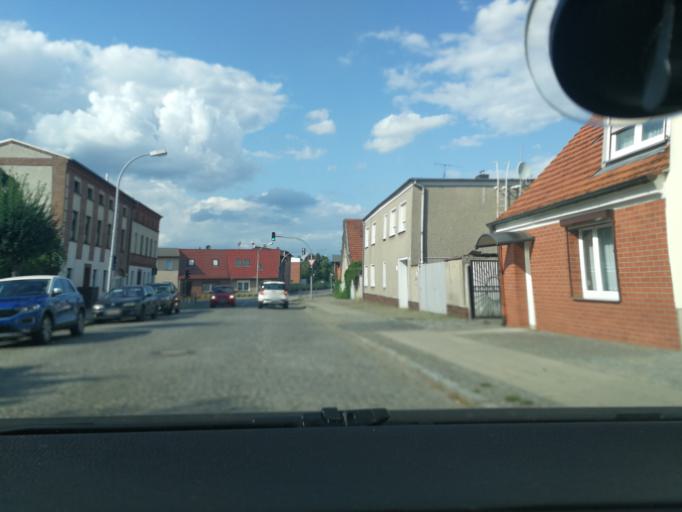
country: DE
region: Brandenburg
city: Pritzwalk
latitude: 53.1497
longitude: 12.1846
